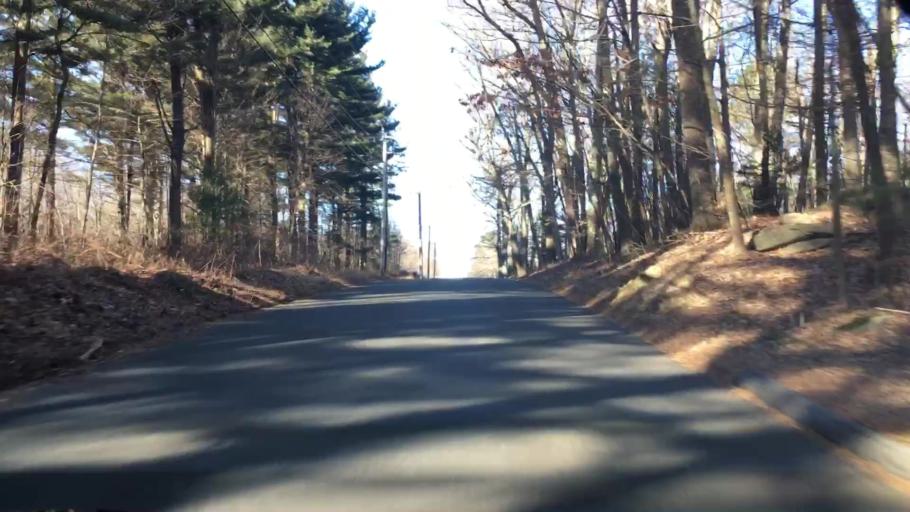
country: US
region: Connecticut
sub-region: Tolland County
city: Crystal Lake
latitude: 41.9549
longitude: -72.4028
